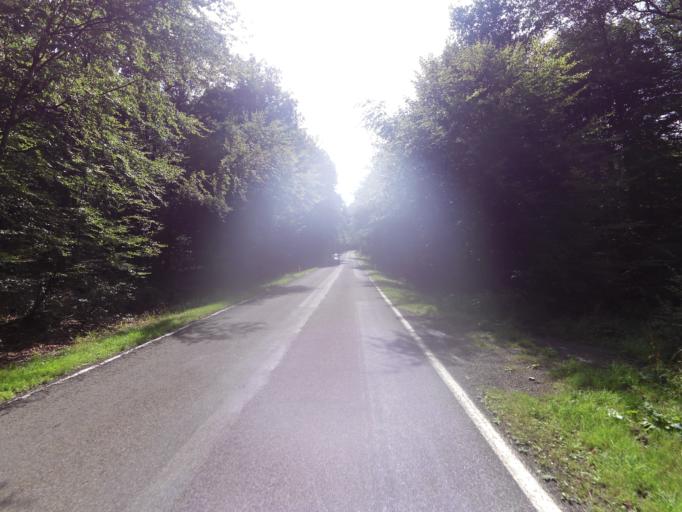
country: BE
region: Wallonia
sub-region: Province du Luxembourg
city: Saint-Hubert
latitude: 50.0612
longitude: 5.3459
